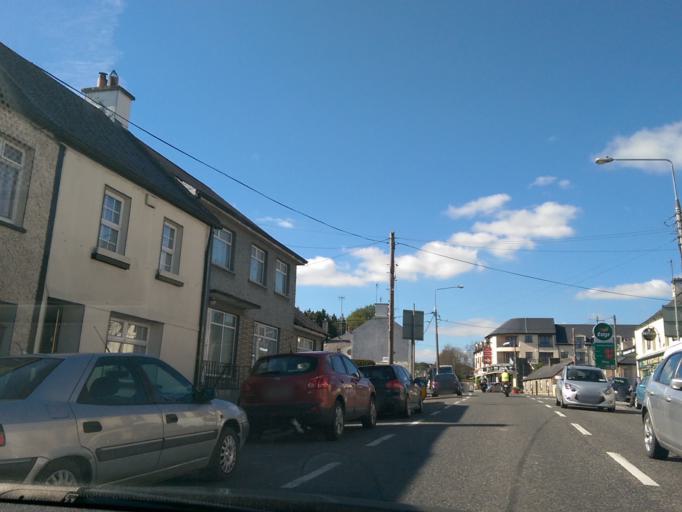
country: IE
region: Leinster
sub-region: Laois
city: Stradbally
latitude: 53.0166
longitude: -7.1498
